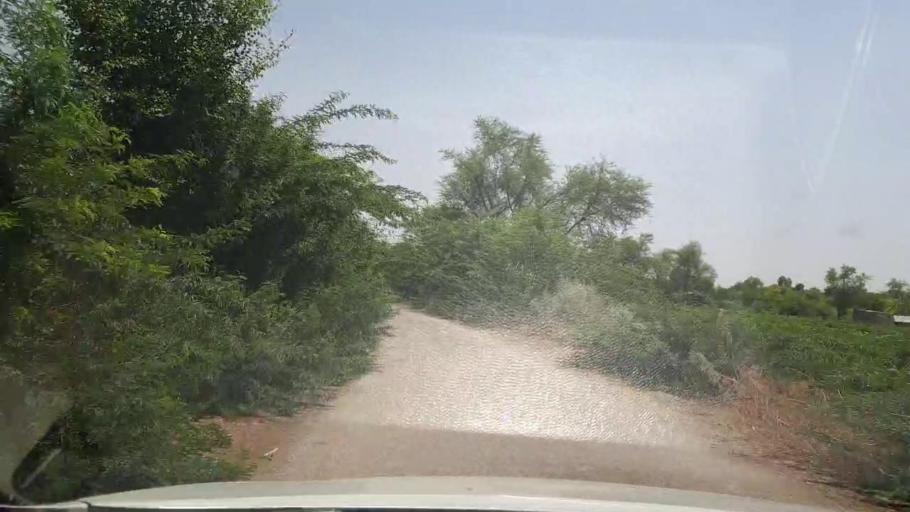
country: PK
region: Sindh
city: Bozdar
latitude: 27.2033
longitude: 68.6770
